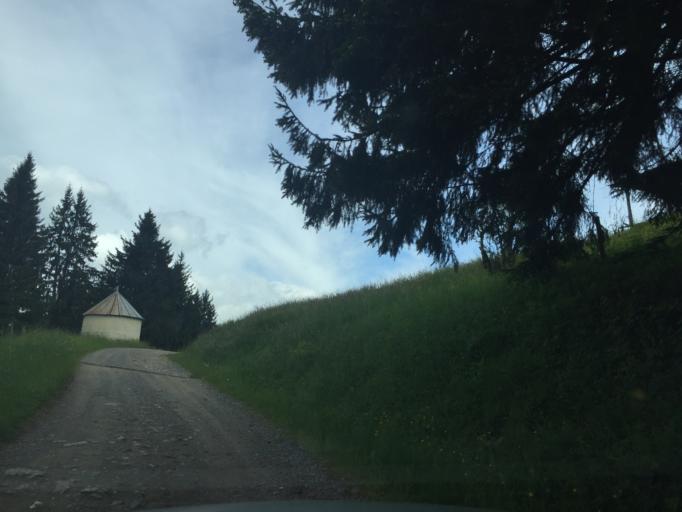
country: FR
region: Rhone-Alpes
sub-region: Departement de la Savoie
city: La Rochette
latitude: 45.4440
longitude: 6.1696
